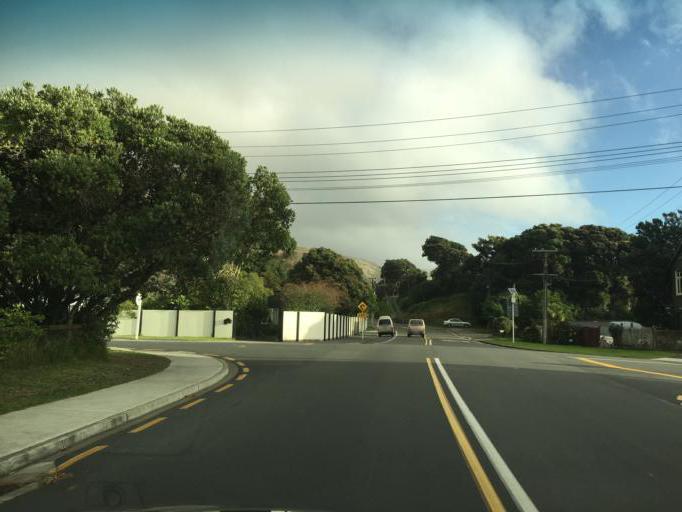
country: NZ
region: Wellington
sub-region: Kapiti Coast District
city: Paraparaumu
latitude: -40.9825
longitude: 174.9564
